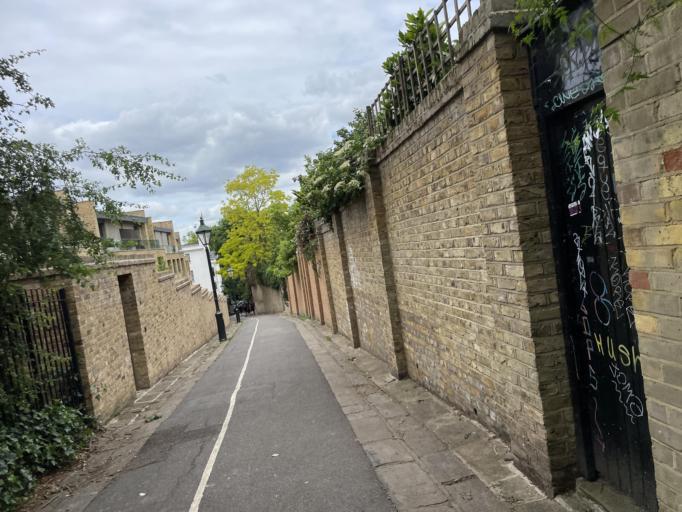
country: GB
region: England
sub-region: Greater London
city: Kensington
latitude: 51.5064
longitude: -0.2032
